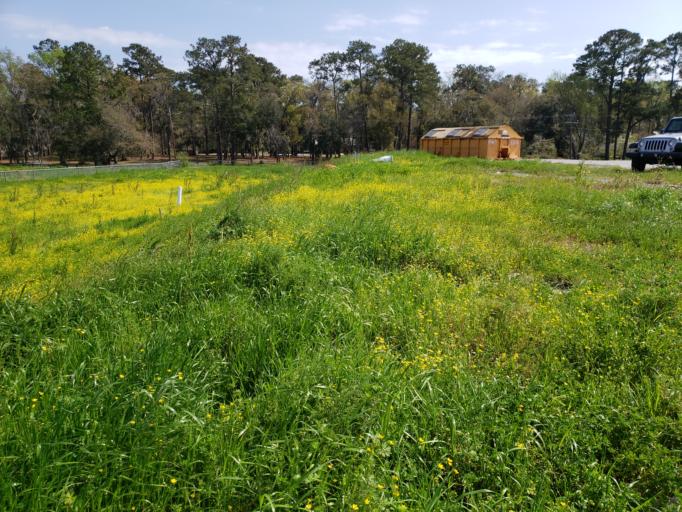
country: US
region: Georgia
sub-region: Chatham County
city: Wilmington Island
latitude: 32.0187
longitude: -80.9711
